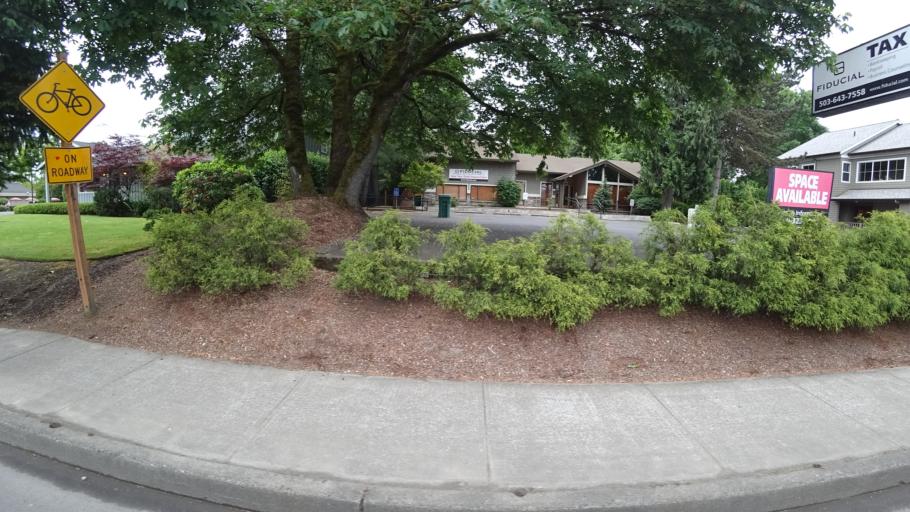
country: US
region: Oregon
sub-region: Washington County
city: Raleigh Hills
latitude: 45.4864
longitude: -122.7751
